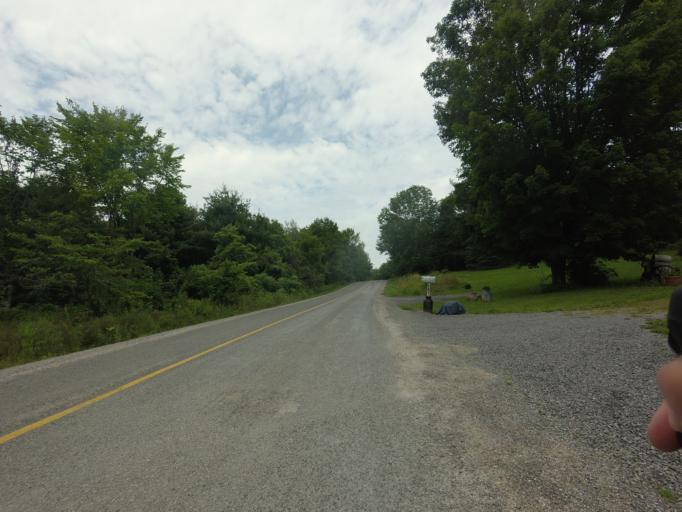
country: CA
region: Ontario
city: Kingston
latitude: 44.6461
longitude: -76.6527
